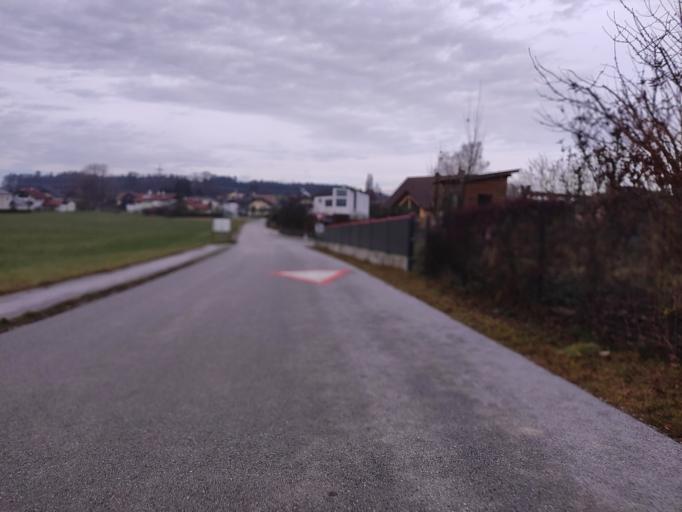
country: AT
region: Salzburg
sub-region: Politischer Bezirk Salzburg-Umgebung
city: Berndorf bei Salzburg
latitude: 48.0054
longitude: 13.0865
